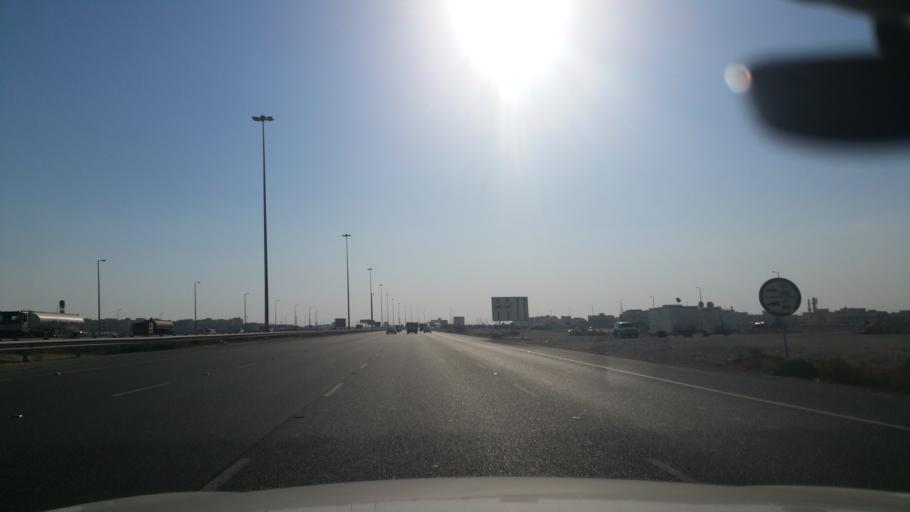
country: QA
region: Baladiyat ar Rayyan
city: Ar Rayyan
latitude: 25.1922
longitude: 51.3739
